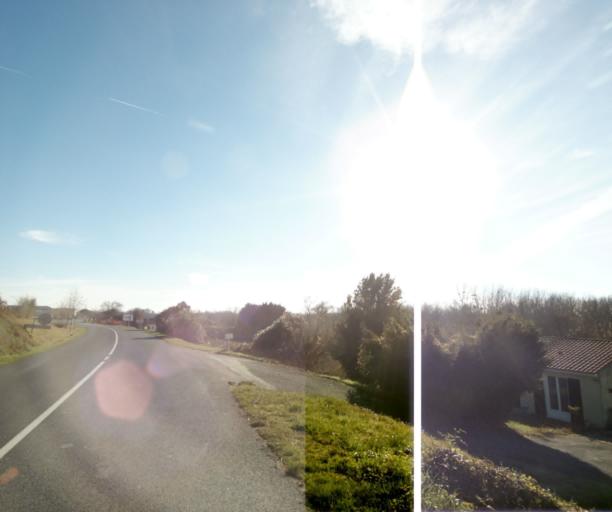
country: FR
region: Poitou-Charentes
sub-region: Departement de la Charente-Maritime
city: Chaniers
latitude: 45.7236
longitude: -0.5706
